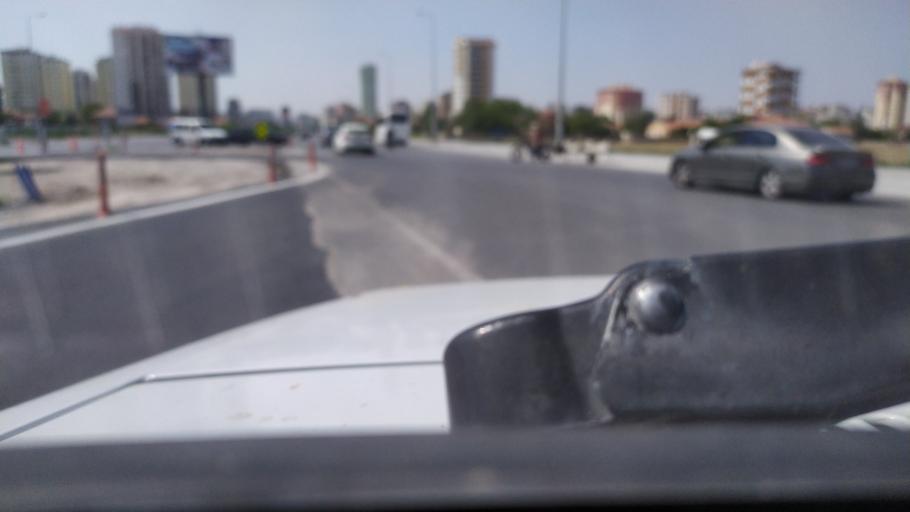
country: TR
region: Kayseri
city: Talas
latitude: 38.7202
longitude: 35.5472
